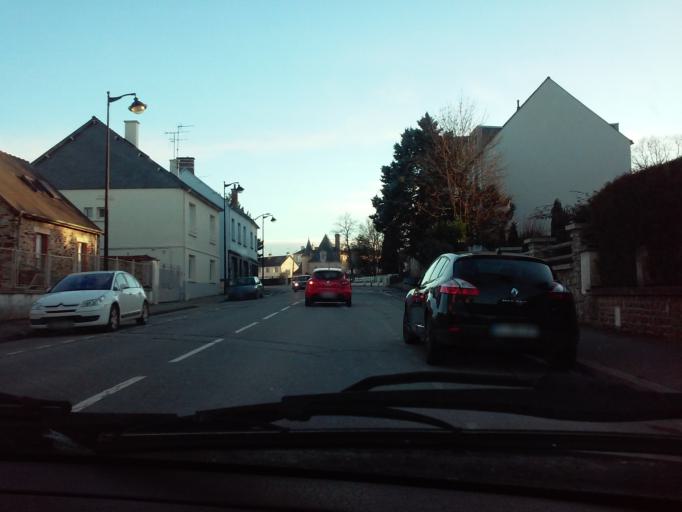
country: FR
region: Brittany
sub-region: Departement d'Ille-et-Vilaine
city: Vitre
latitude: 48.1146
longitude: -1.2104
